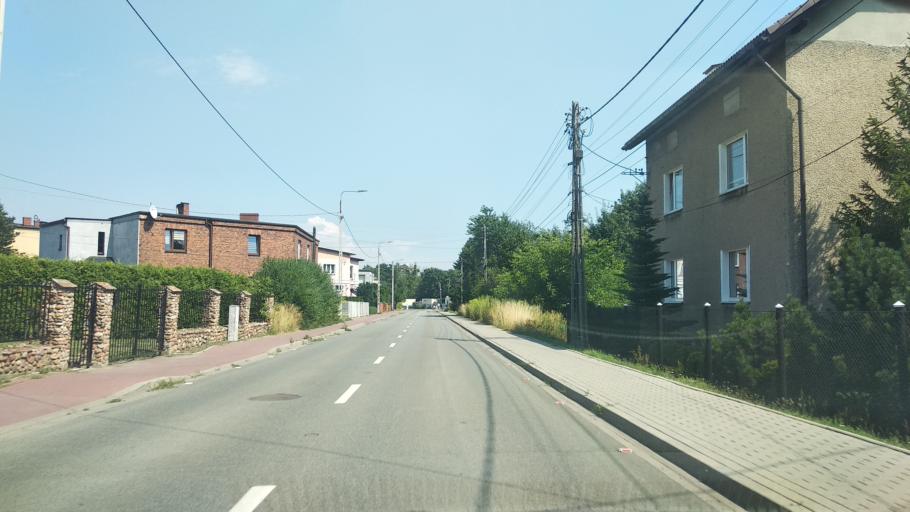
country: PL
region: Silesian Voivodeship
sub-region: Powiat tarnogorski
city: Radzionkow
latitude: 50.3948
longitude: 18.8924
